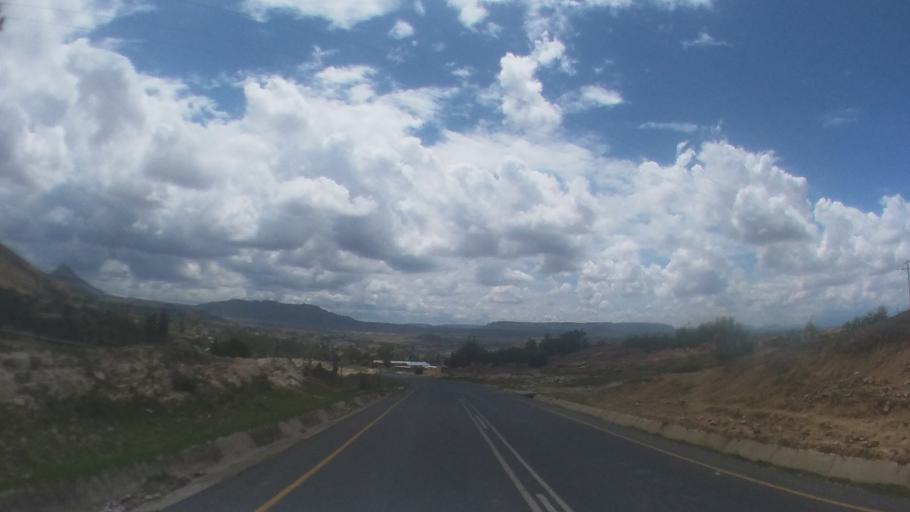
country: LS
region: Maseru
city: Maseru
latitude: -29.4237
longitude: 27.4697
